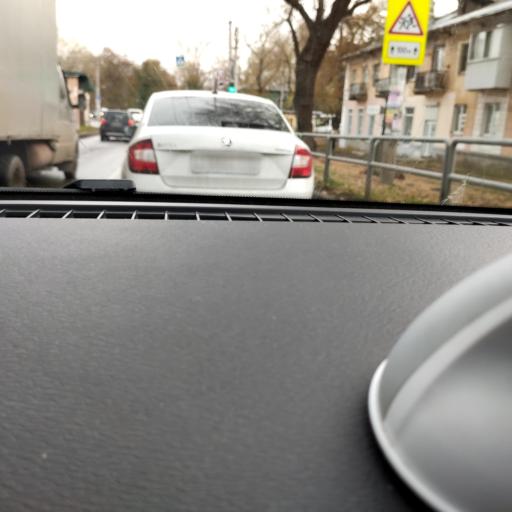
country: RU
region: Samara
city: Samara
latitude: 53.2246
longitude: 50.2547
